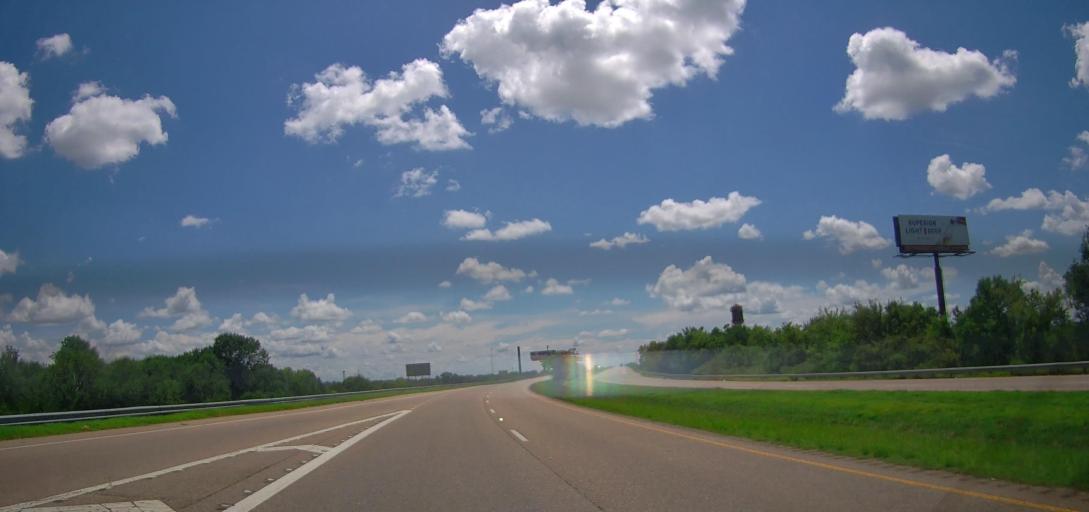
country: US
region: Alabama
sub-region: Montgomery County
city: Montgomery
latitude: 32.4007
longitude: -86.3105
